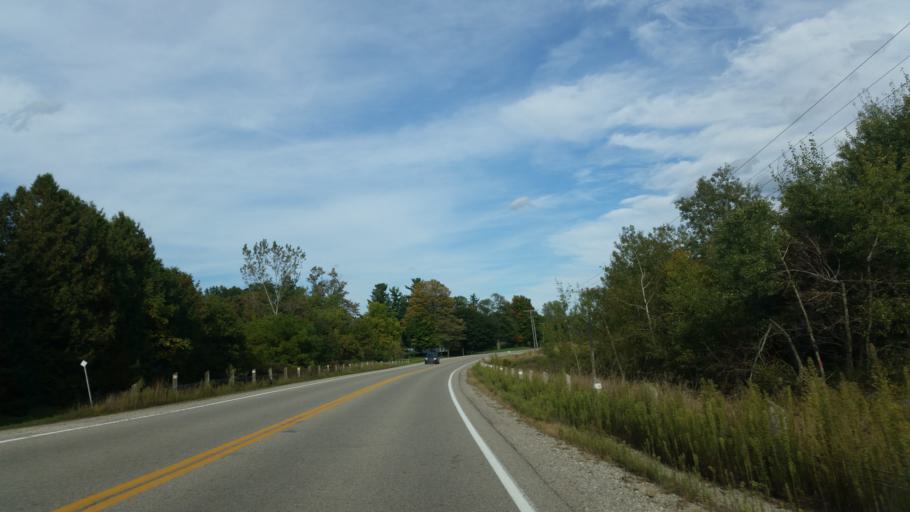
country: CA
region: Ontario
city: Delaware
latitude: 42.8781
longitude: -81.4710
